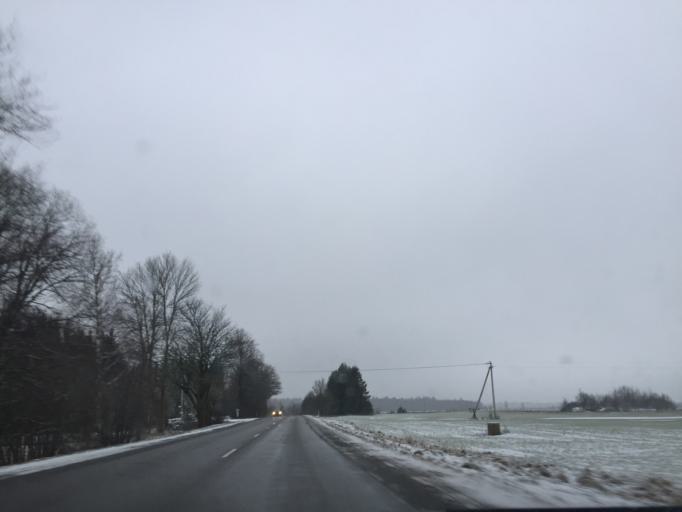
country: EE
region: Laeaene
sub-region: Lihula vald
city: Lihula
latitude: 58.5596
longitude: 23.9870
